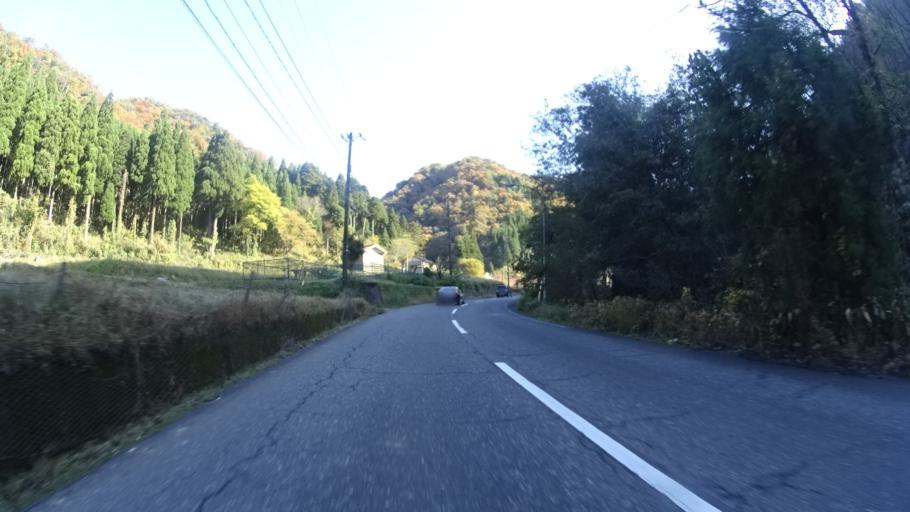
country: JP
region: Ishikawa
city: Tsurugi-asahimachi
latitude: 36.3742
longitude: 136.5659
